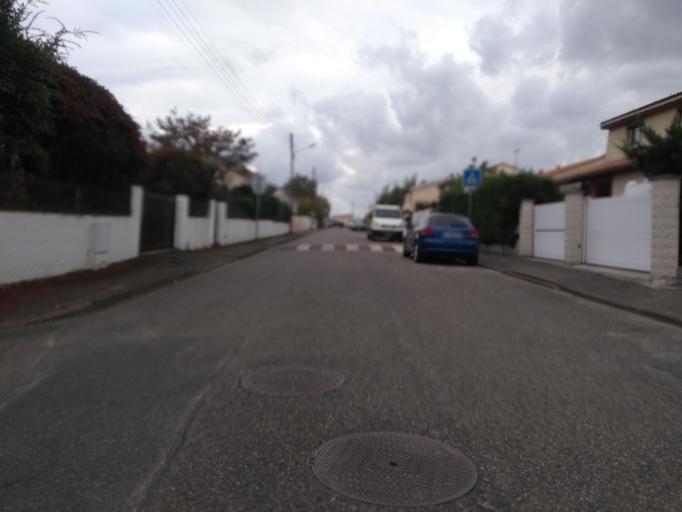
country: FR
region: Aquitaine
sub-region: Departement de la Gironde
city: Pessac
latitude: 44.8254
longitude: -0.6605
